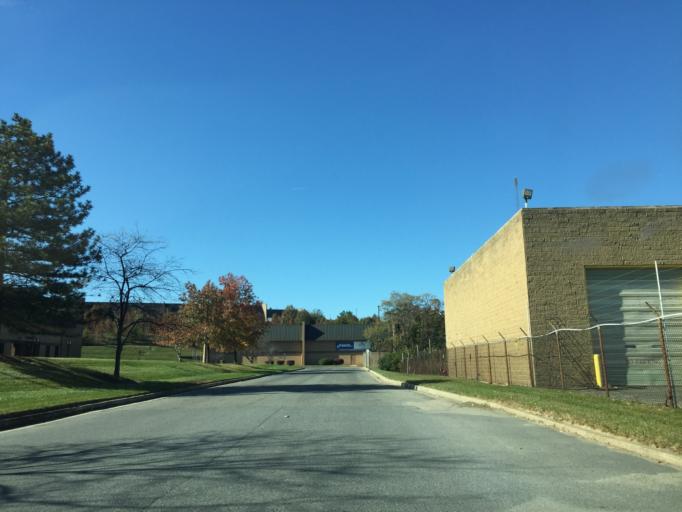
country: US
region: Maryland
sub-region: Baltimore County
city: Lansdowne
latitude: 39.2517
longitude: -76.6705
